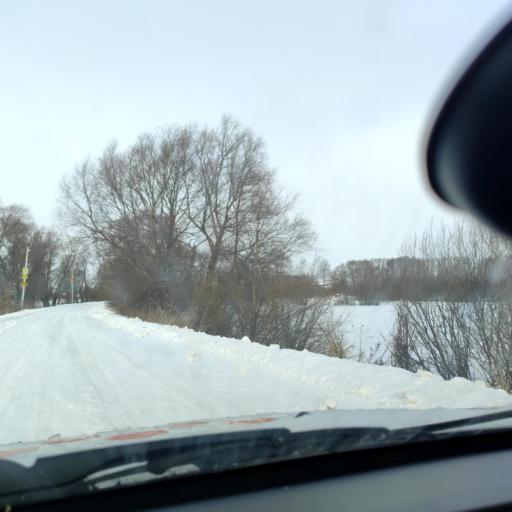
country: RU
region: Bashkortostan
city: Mikhaylovka
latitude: 54.8683
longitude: 55.7518
